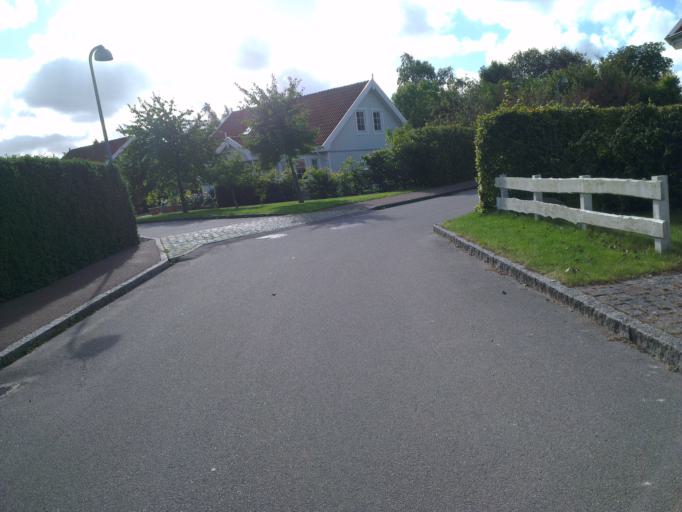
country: DK
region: Capital Region
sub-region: Frederikssund Kommune
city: Slangerup
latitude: 55.8406
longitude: 12.1705
